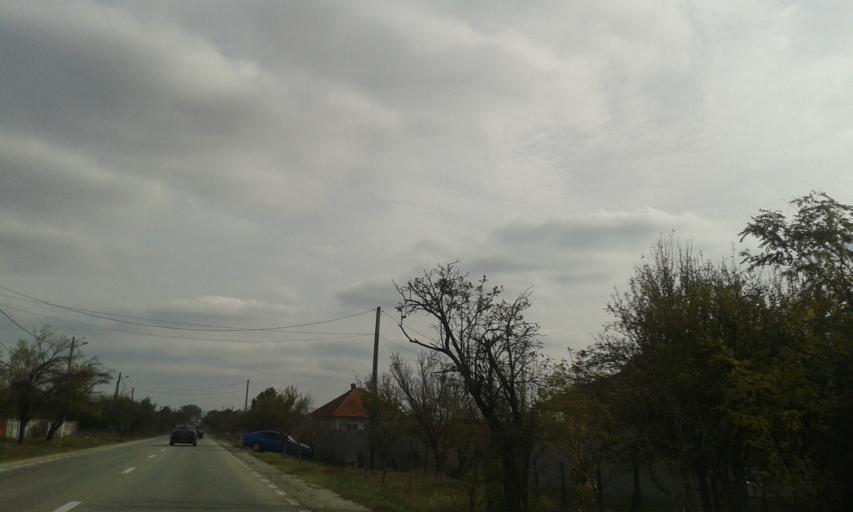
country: RO
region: Gorj
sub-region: Comuna Scoarta
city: Scoarta
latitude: 45.0285
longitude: 23.4266
